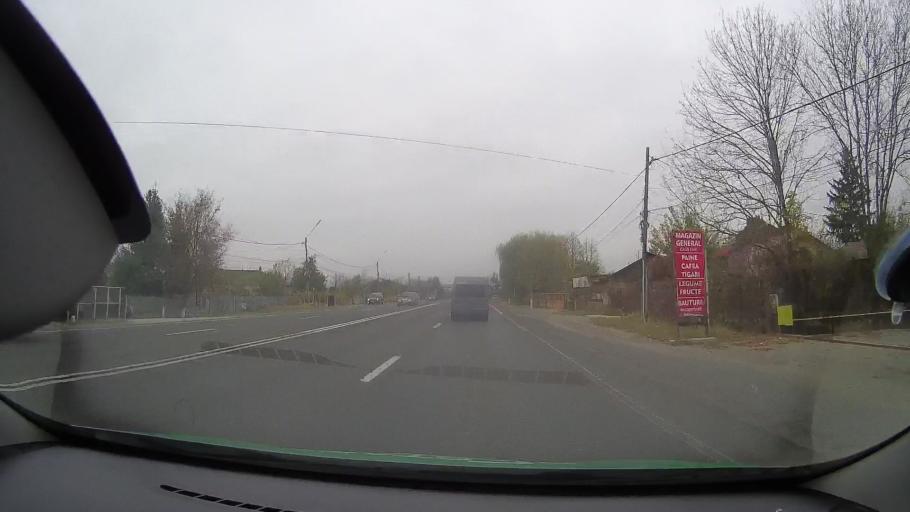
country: RO
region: Ilfov
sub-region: Comuna Ciolpani
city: Ciolpani
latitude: 44.7291
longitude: 26.1109
